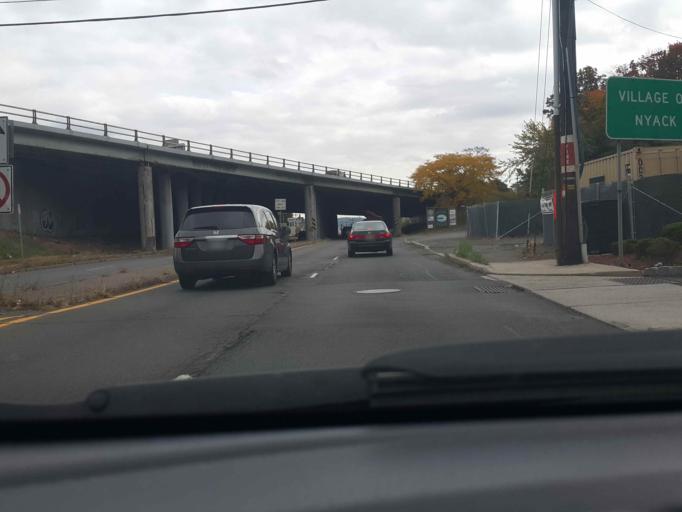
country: US
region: New York
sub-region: Rockland County
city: Nyack
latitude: 41.0934
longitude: -73.9326
